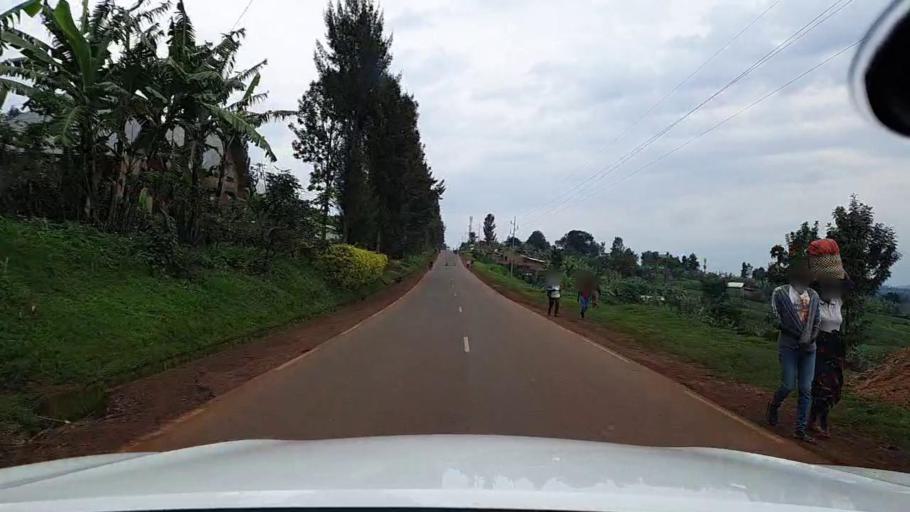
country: RW
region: Western Province
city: Cyangugu
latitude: -2.6220
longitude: 28.9467
